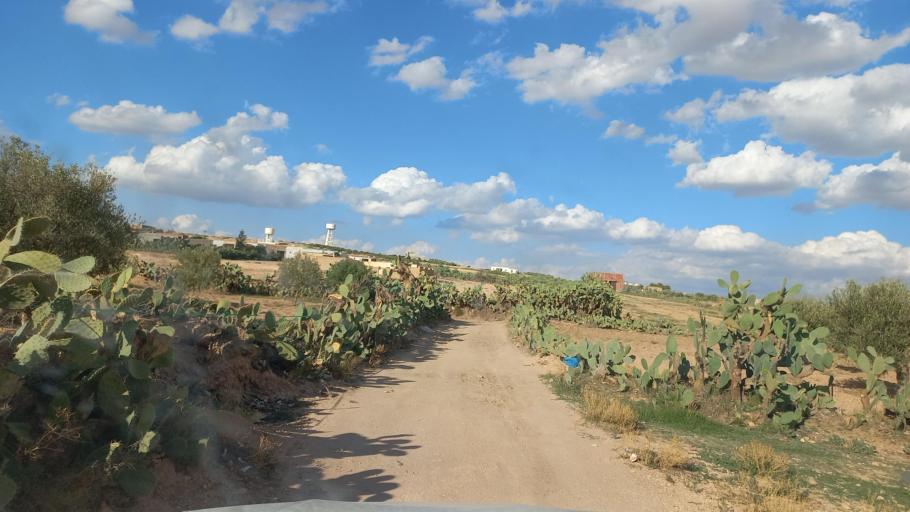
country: TN
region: Al Qasrayn
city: Sbiba
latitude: 35.3860
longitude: 9.0435
